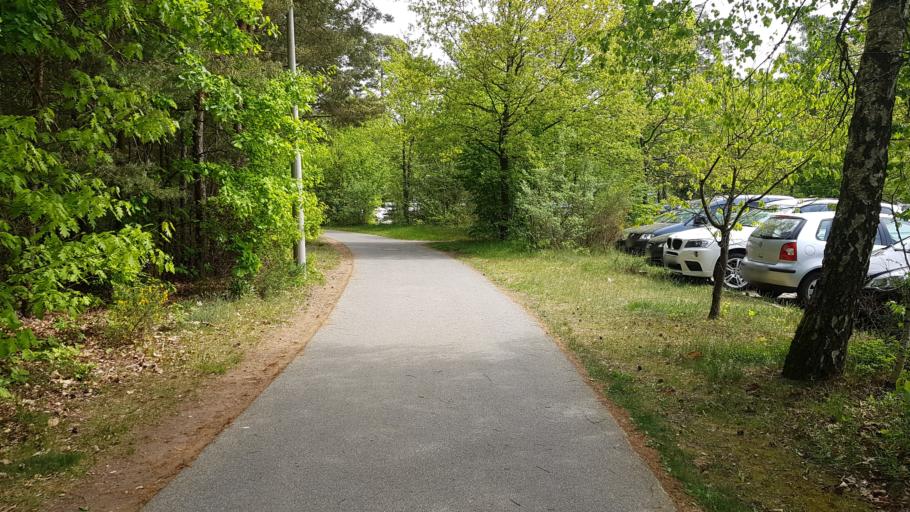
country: DE
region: Bavaria
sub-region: Regierungsbezirk Mittelfranken
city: Schwarzenbruck
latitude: 49.3621
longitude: 11.2613
